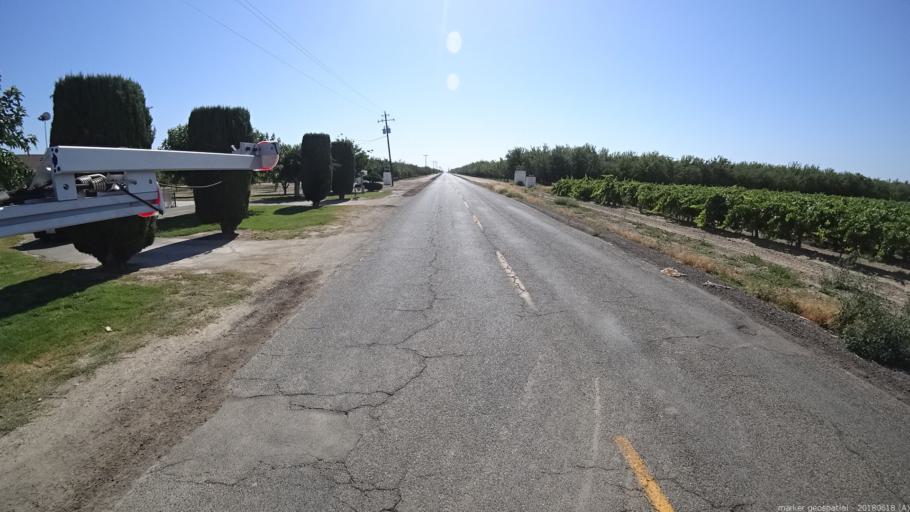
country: US
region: California
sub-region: Madera County
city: Parkwood
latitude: 36.8367
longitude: -120.1607
